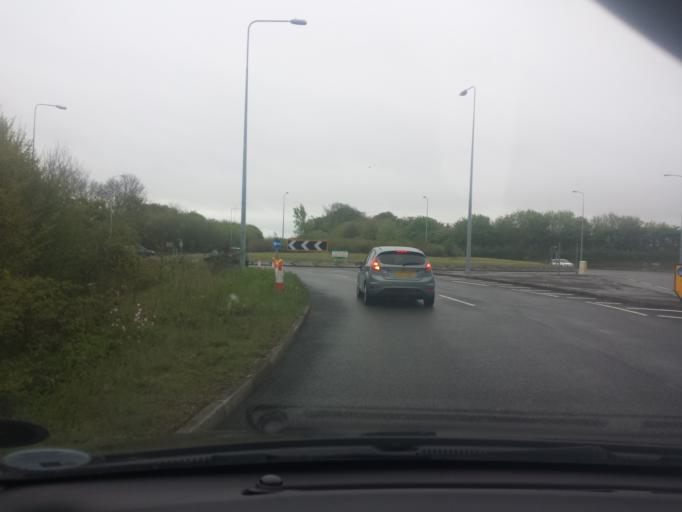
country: GB
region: England
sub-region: Essex
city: Little Clacton
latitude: 51.8201
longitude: 1.1359
